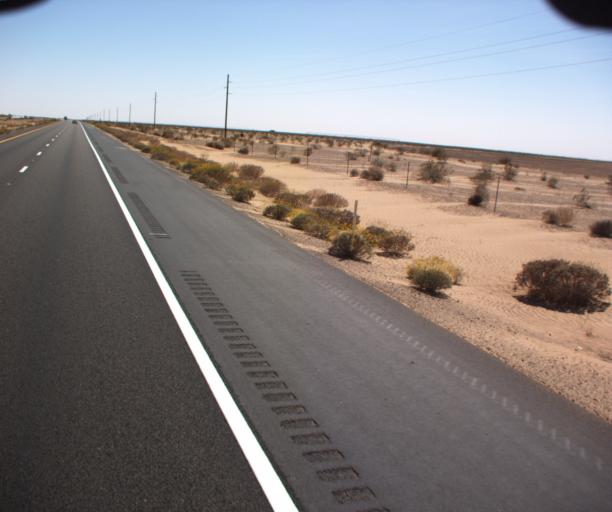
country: US
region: Arizona
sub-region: Yuma County
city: Somerton
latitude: 32.5239
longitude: -114.5621
